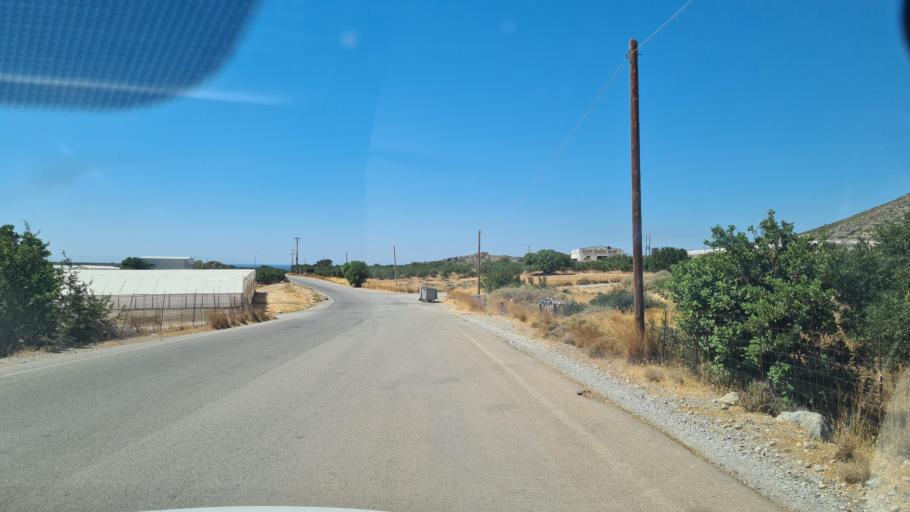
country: GR
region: Crete
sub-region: Nomos Chanias
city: Palaiochora
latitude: 35.2883
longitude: 23.5488
